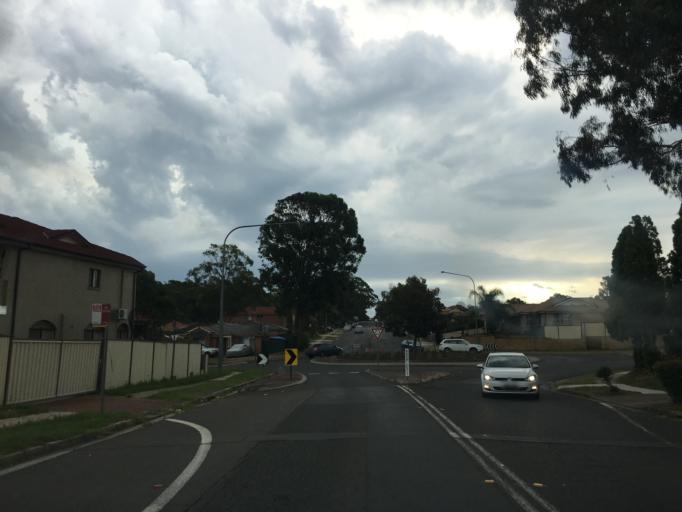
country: AU
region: New South Wales
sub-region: Liverpool
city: Miller
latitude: -33.9108
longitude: 150.8724
